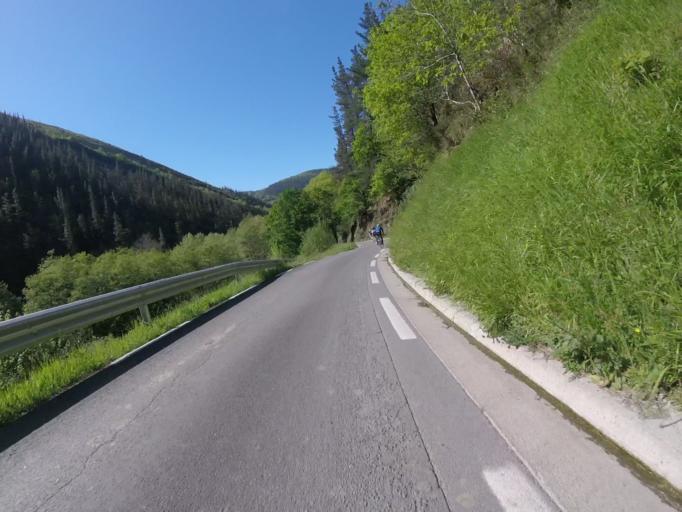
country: ES
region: Basque Country
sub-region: Provincia de Guipuzcoa
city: Errezil
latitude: 43.1821
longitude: -2.2025
